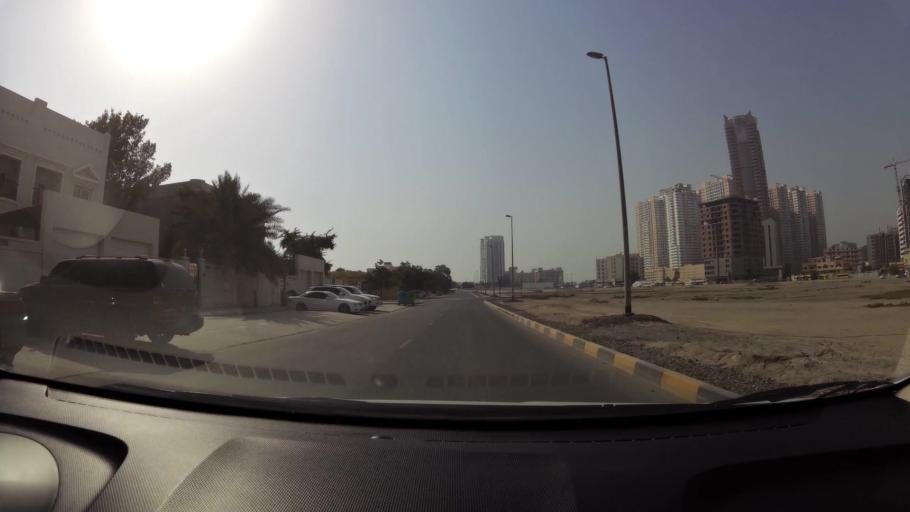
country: AE
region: Ajman
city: Ajman
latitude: 25.3891
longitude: 55.4311
